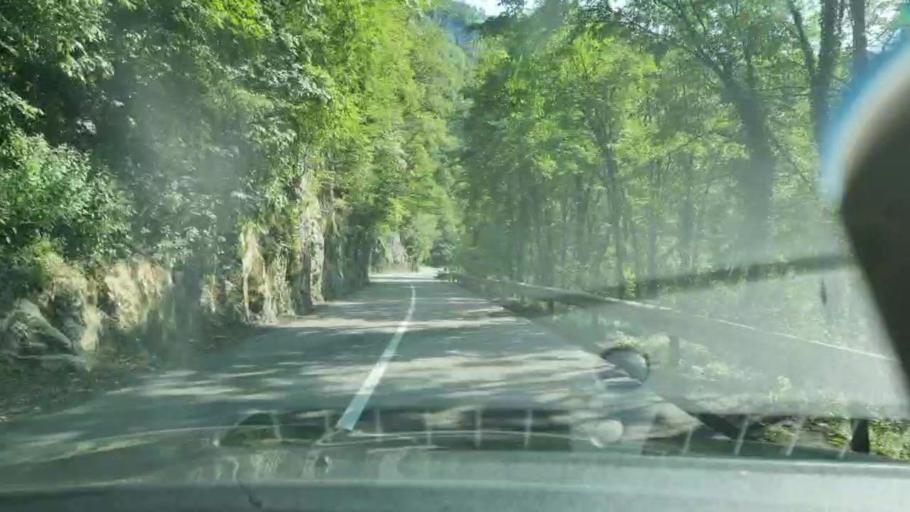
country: BA
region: Federation of Bosnia and Herzegovina
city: Bosanska Krupa
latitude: 44.8682
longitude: 16.0965
